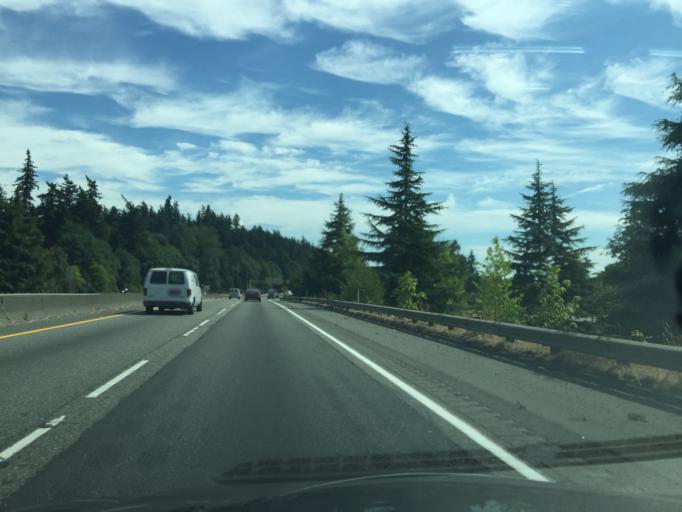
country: US
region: Washington
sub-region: Skagit County
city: Mount Vernon
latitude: 48.4173
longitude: -122.3329
